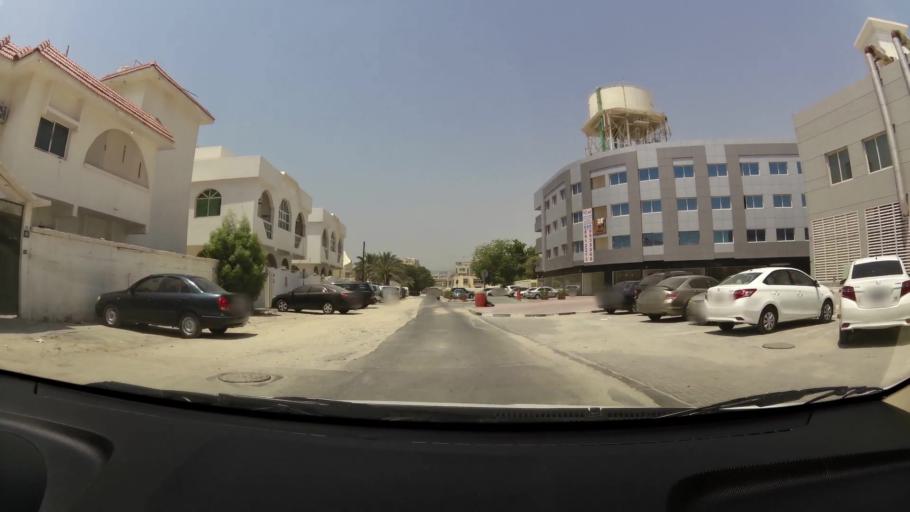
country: AE
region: Ajman
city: Ajman
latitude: 25.4012
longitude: 55.4335
